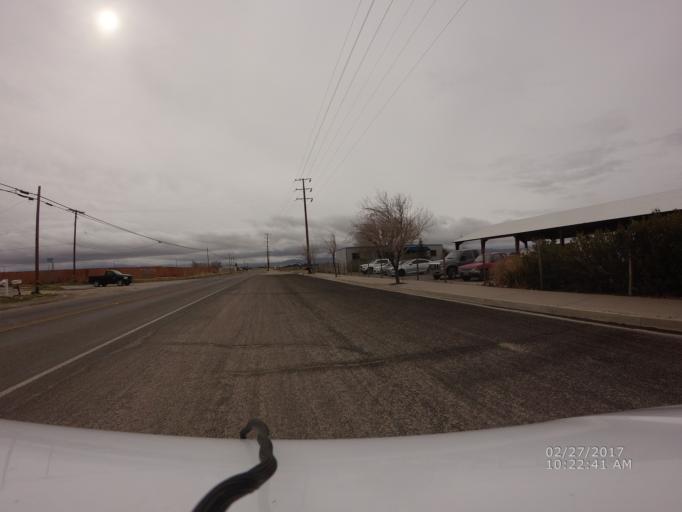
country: US
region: California
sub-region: Los Angeles County
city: Lancaster
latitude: 34.7280
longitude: -118.1308
